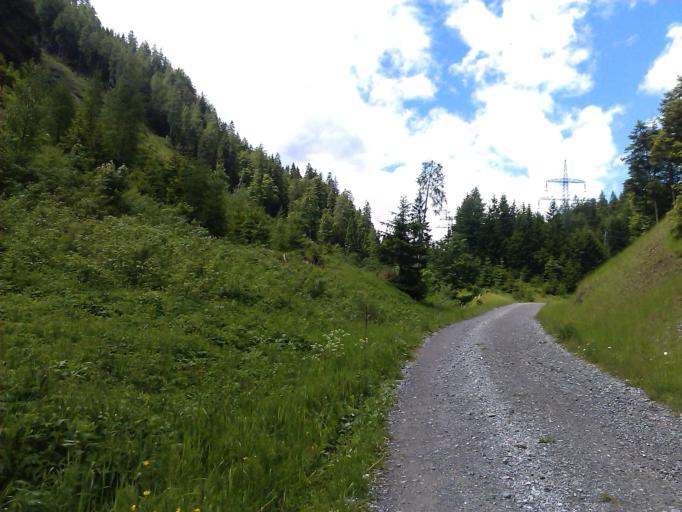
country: AT
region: Tyrol
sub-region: Politischer Bezirk Imst
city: Nassereith
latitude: 47.3533
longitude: 10.8510
